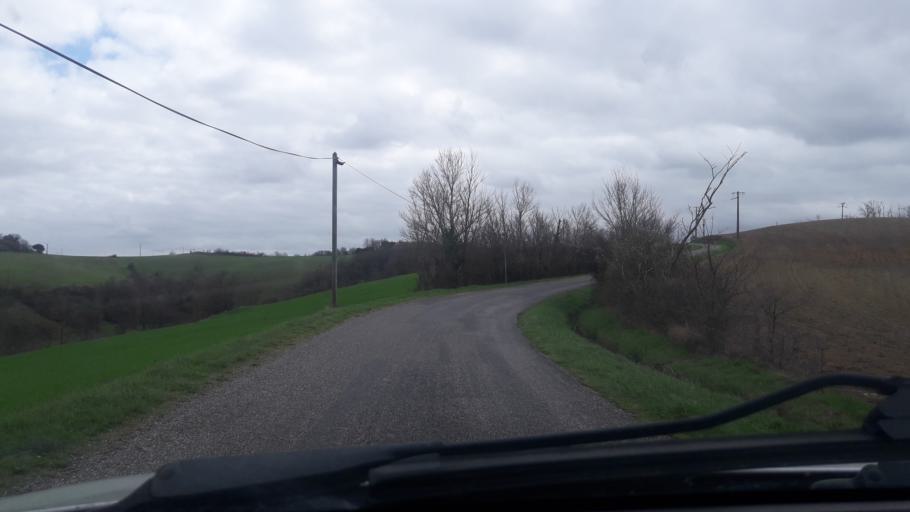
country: FR
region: Midi-Pyrenees
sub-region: Departement de la Haute-Garonne
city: Montesquieu-Volvestre
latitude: 43.2058
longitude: 1.3080
